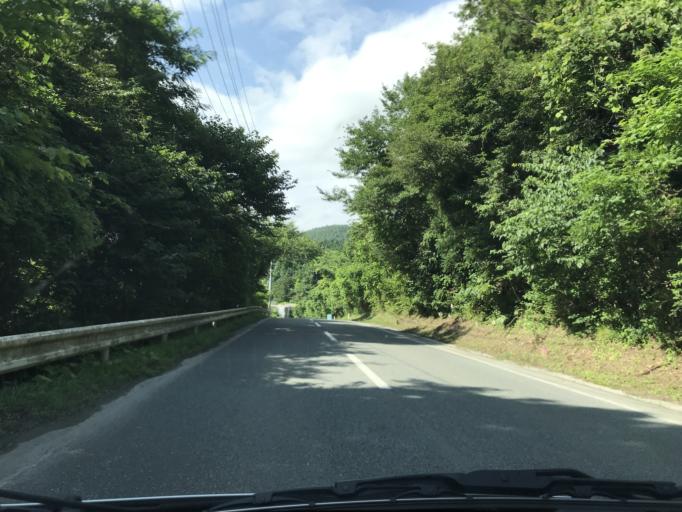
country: JP
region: Iwate
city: Ichinoseki
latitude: 39.0032
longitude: 141.2682
